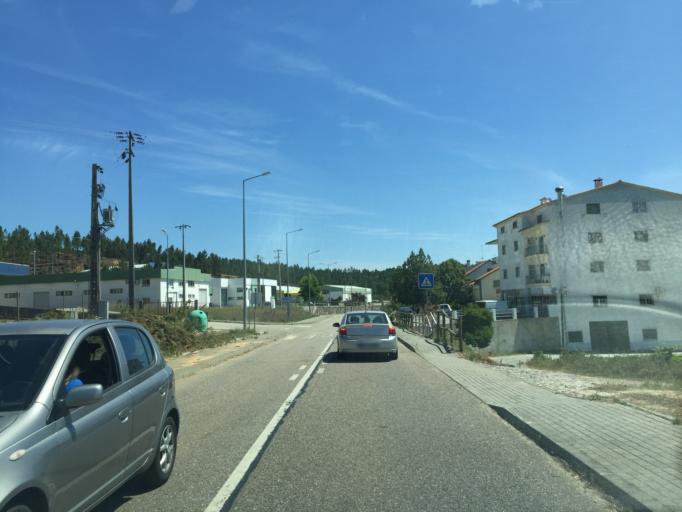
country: PT
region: Castelo Branco
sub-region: Oleiros
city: Oleiros
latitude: 39.9222
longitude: -7.9000
